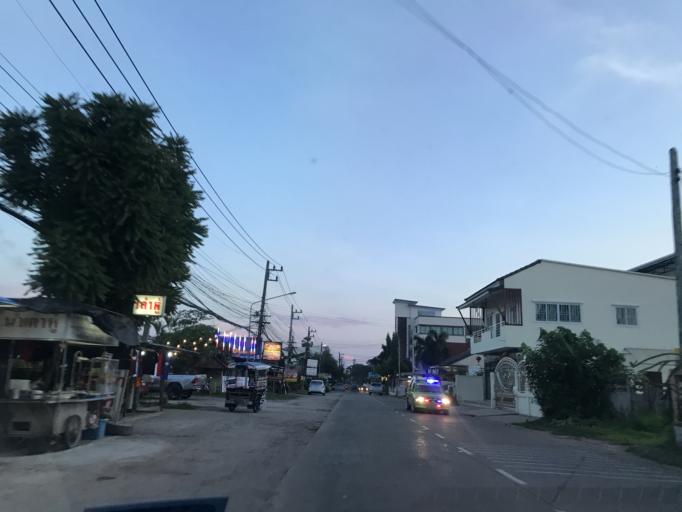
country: TH
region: Changwat Udon Thani
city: Udon Thani
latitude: 17.4016
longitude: 102.7728
